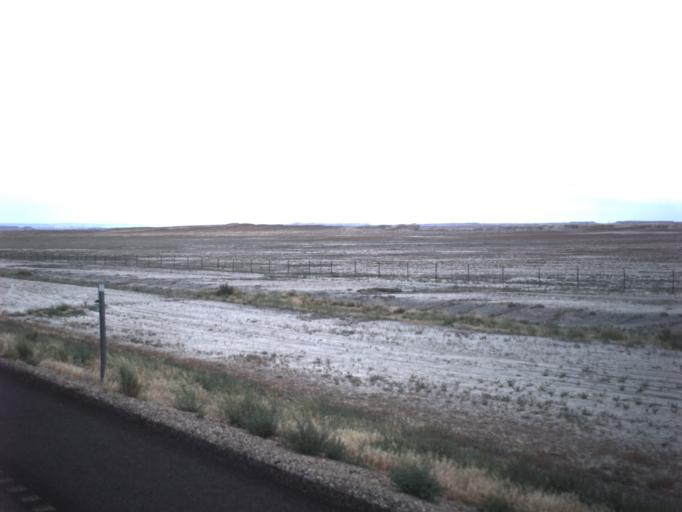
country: US
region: Utah
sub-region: Carbon County
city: East Carbon City
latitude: 38.9978
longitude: -110.2626
